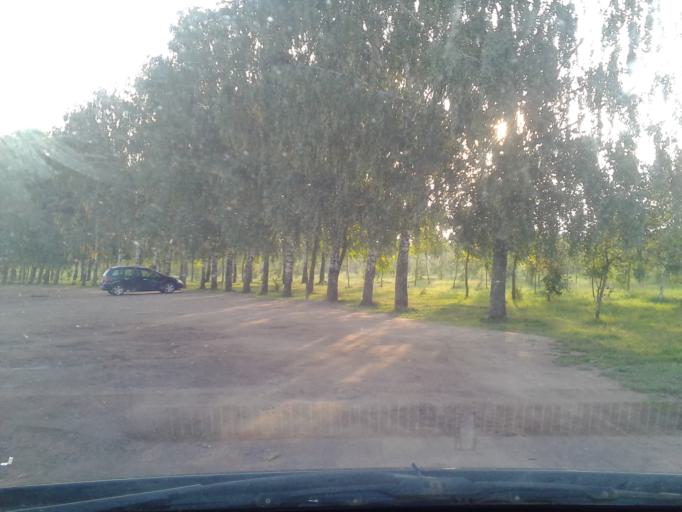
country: BY
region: Minsk
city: Bal'shavik
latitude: 53.9529
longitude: 27.5827
